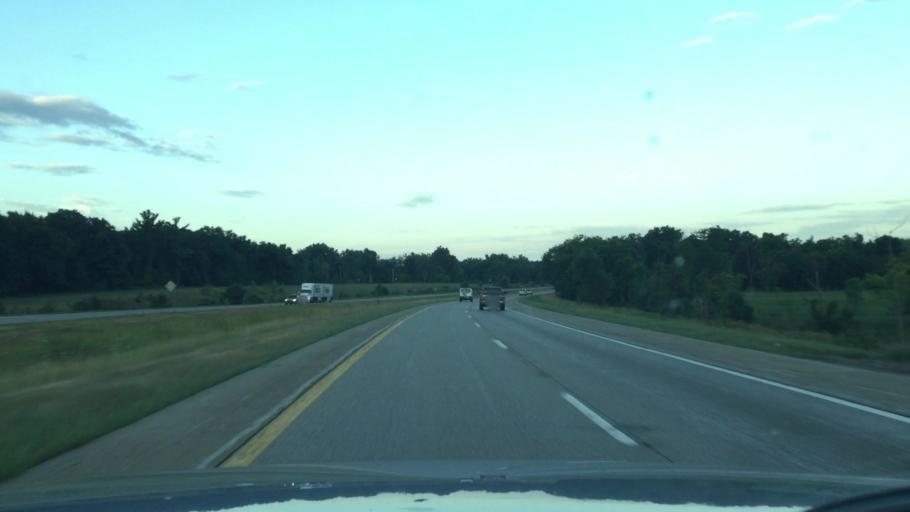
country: US
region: Michigan
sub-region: Shiawassee County
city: Perry
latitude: 42.8192
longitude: -84.2720
